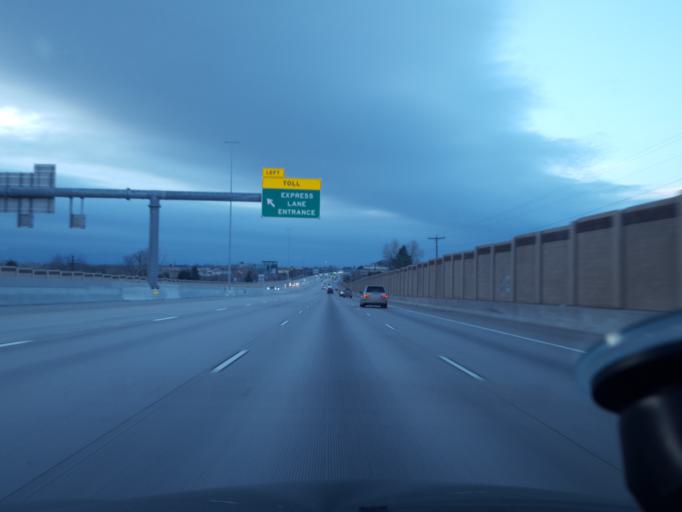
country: US
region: Colorado
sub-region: Adams County
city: Westminster
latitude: 39.8459
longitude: -105.0431
